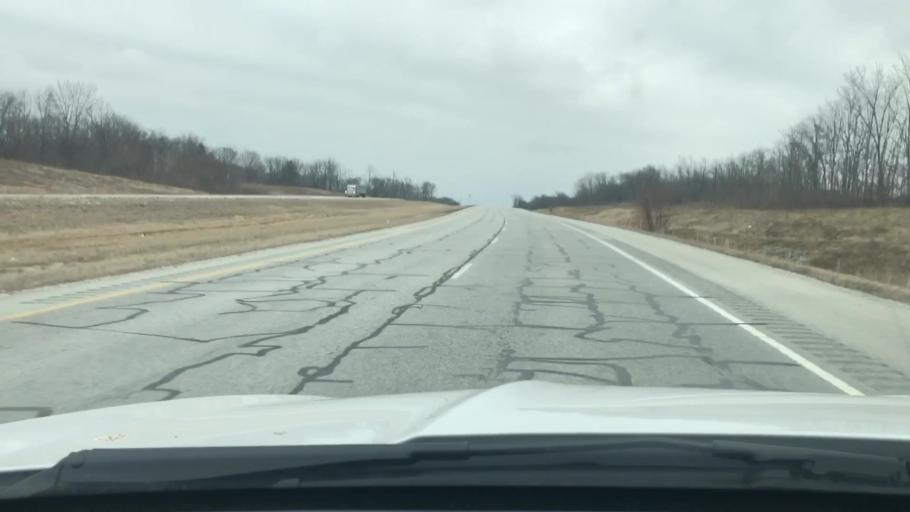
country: US
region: Indiana
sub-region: Carroll County
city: Flora
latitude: 40.6475
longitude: -86.5639
